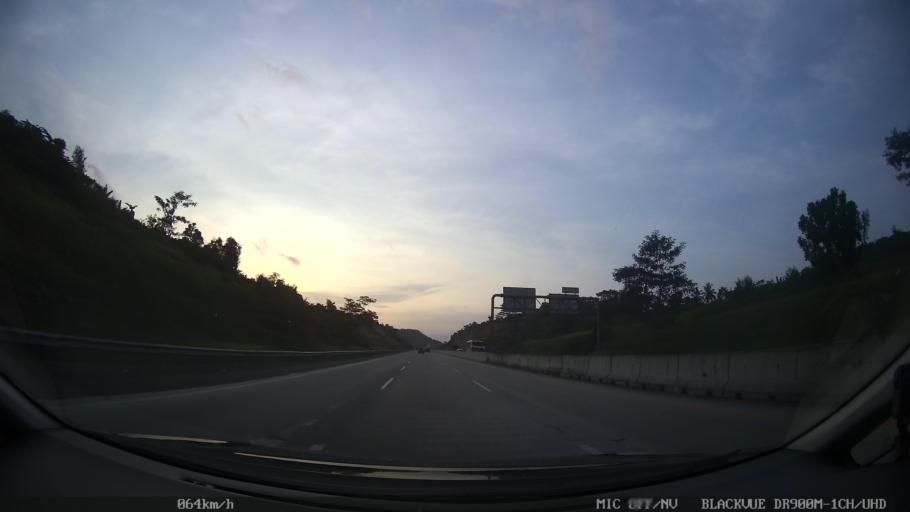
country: ID
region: Lampung
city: Penengahan
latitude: -5.8634
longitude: 105.7420
